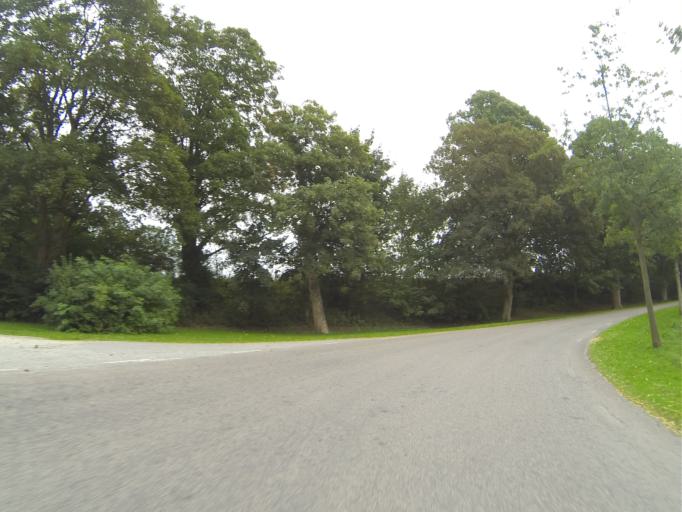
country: SE
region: Skane
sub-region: Eslovs Kommun
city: Eslov
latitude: 55.7676
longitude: 13.2588
